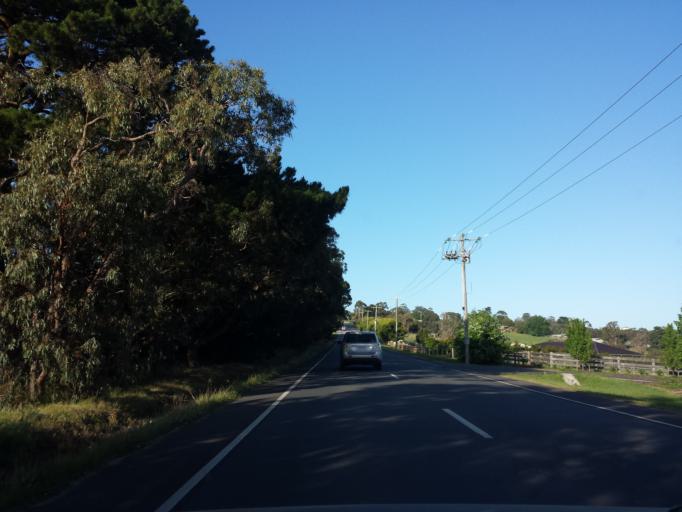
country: AU
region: Victoria
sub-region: Casey
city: Narre Warren North
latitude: -37.9779
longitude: 145.3574
